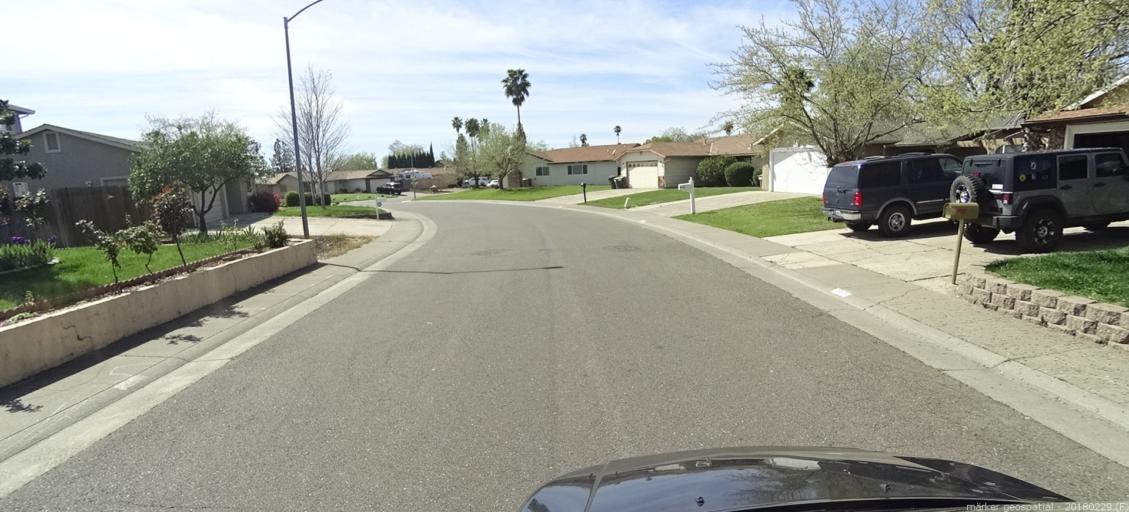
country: US
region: California
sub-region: Sacramento County
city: Rosemont
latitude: 38.5410
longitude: -121.3585
